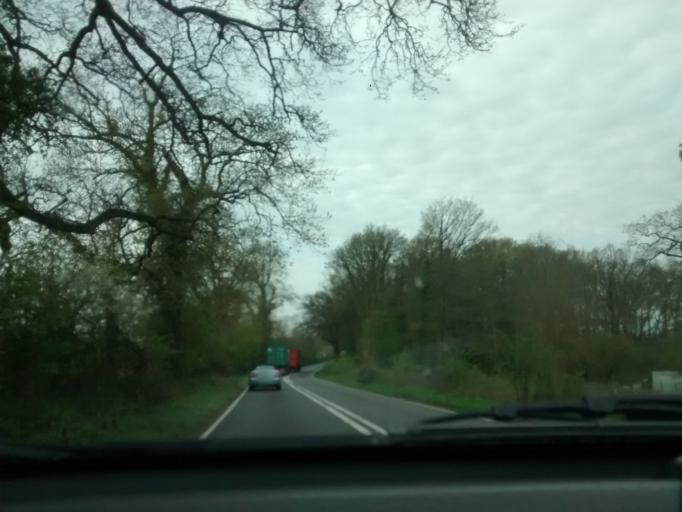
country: GB
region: England
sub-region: Oxfordshire
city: Bicester
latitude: 51.9426
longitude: -1.1201
